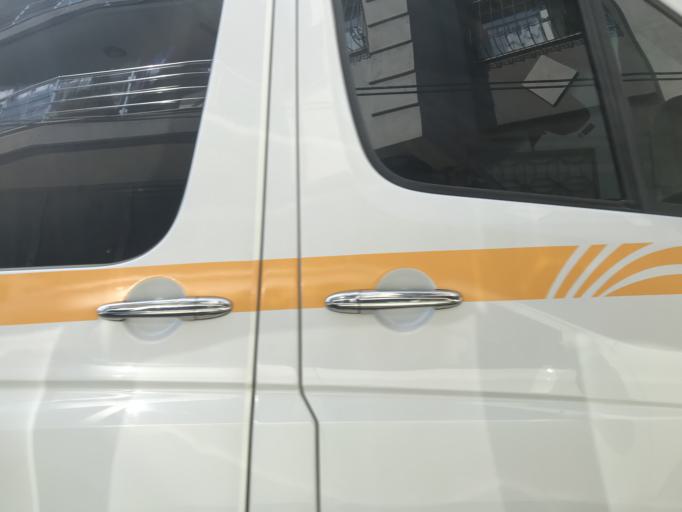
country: TR
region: Izmir
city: Karabaglar
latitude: 38.3879
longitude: 27.1309
